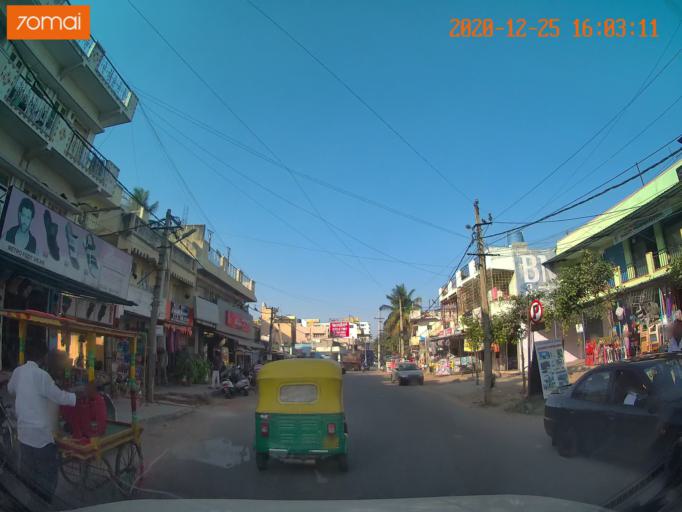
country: IN
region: Karnataka
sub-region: Bangalore Urban
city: Bangalore
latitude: 12.8839
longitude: 77.6248
